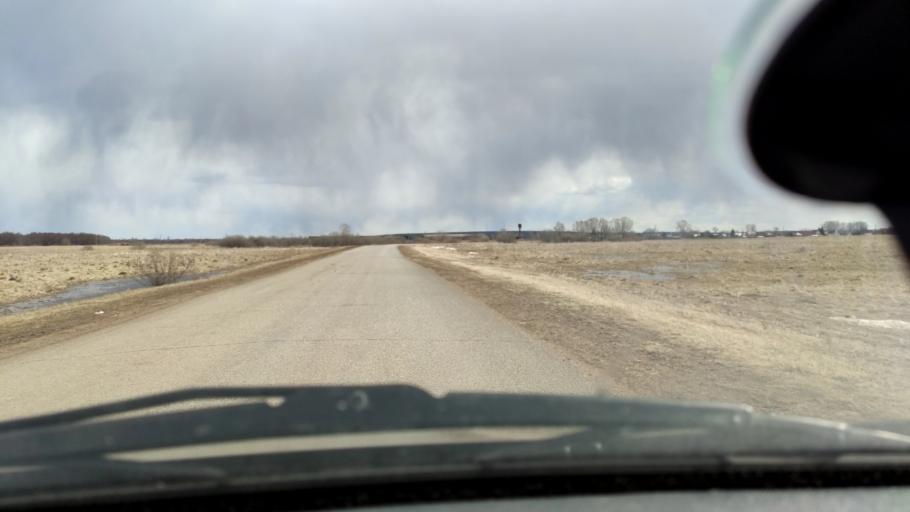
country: RU
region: Bashkortostan
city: Mikhaylovka
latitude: 54.9761
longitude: 55.7788
